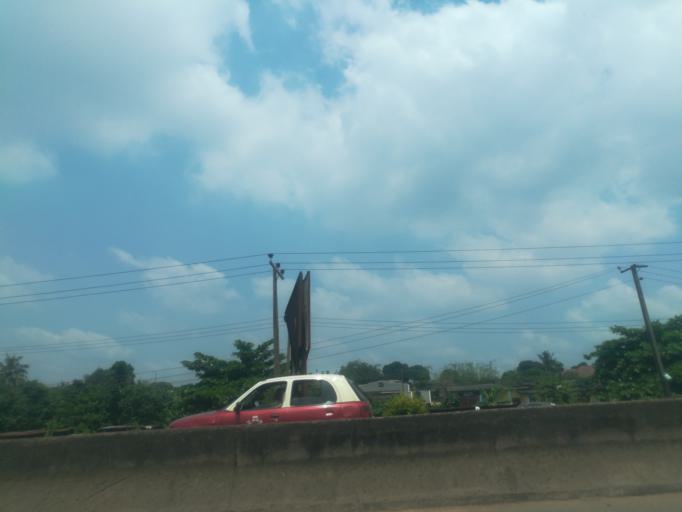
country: NG
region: Oyo
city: Ibadan
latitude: 7.3944
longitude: 3.9602
